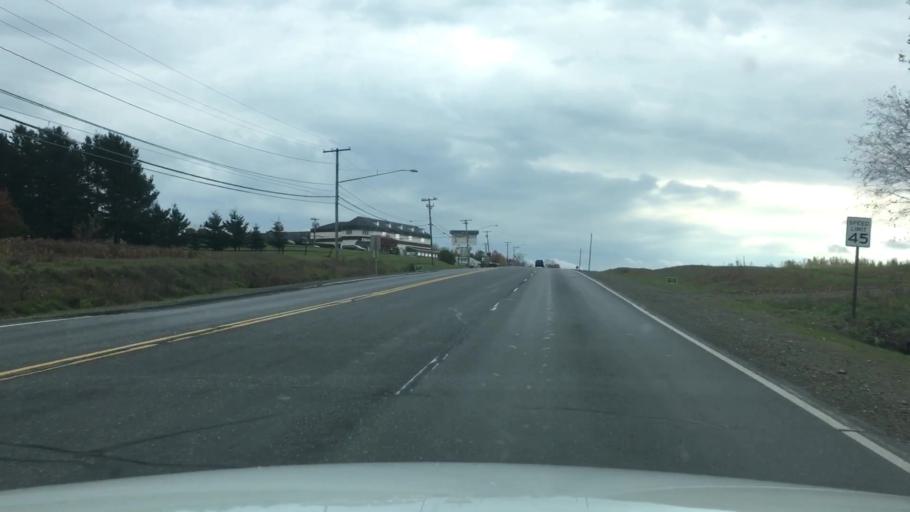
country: US
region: Maine
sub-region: Aroostook County
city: Presque Isle
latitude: 46.6695
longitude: -68.0132
